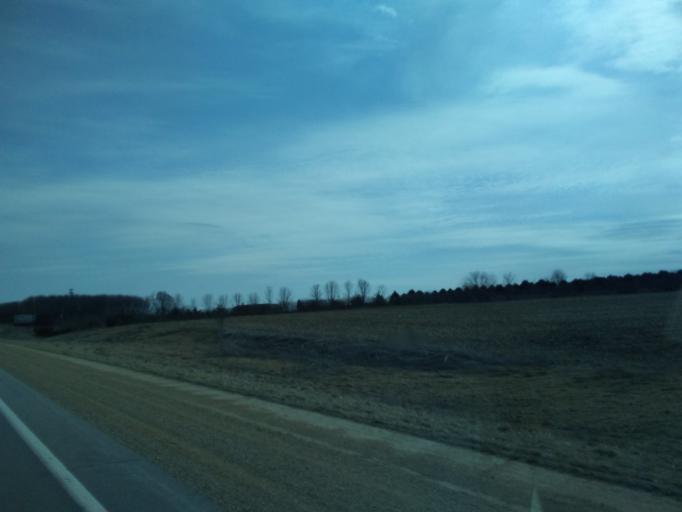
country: US
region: Iowa
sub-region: Winneshiek County
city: Decorah
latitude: 43.3725
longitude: -91.8117
